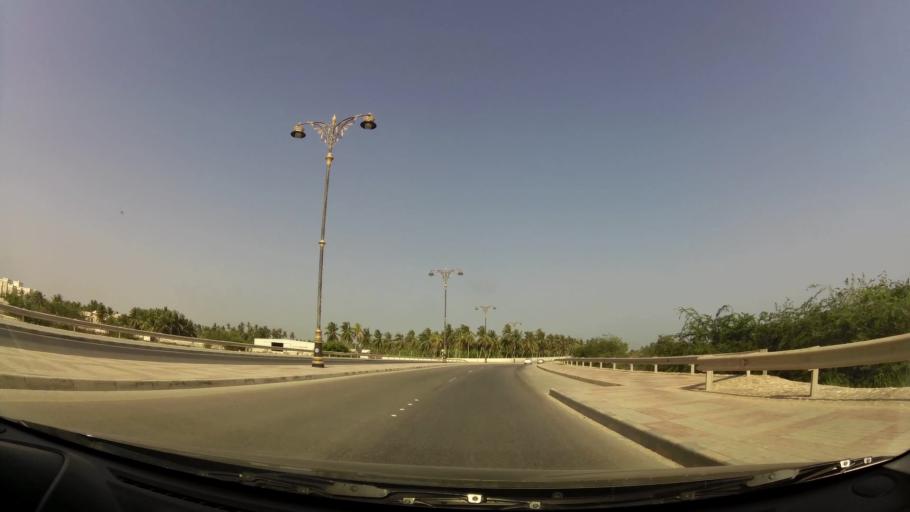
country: OM
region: Zufar
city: Salalah
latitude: 17.0022
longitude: 54.0670
